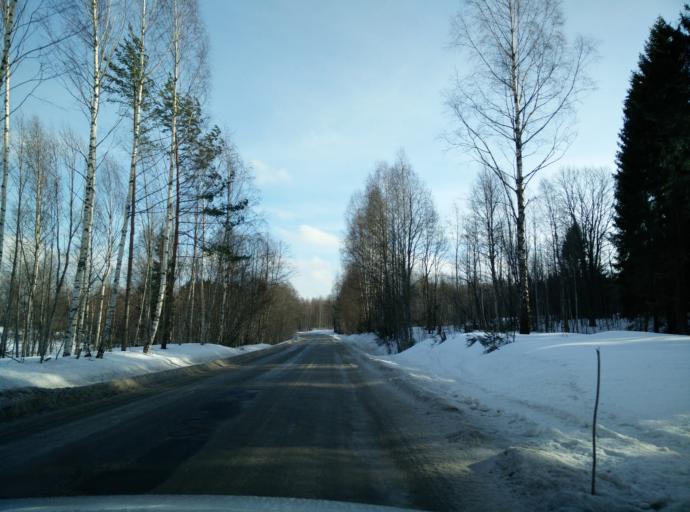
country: SE
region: Vaesternorrland
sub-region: Sundsvalls Kommun
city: Njurundabommen
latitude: 62.2209
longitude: 17.3496
